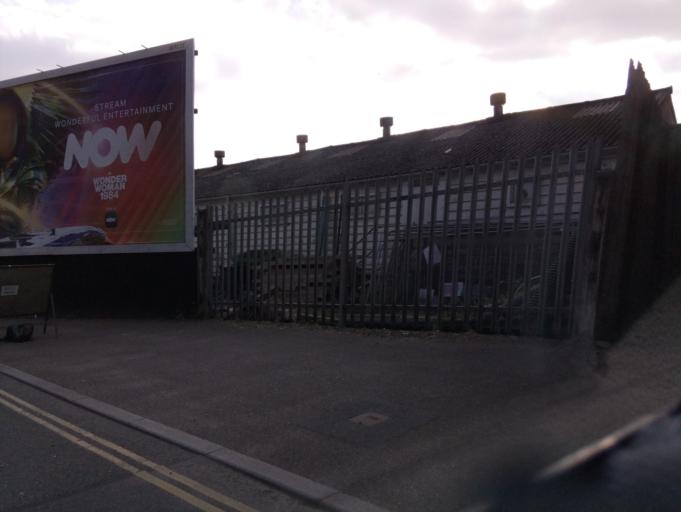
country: GB
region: England
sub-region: Devon
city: Exeter
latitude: 50.7356
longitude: -3.5443
